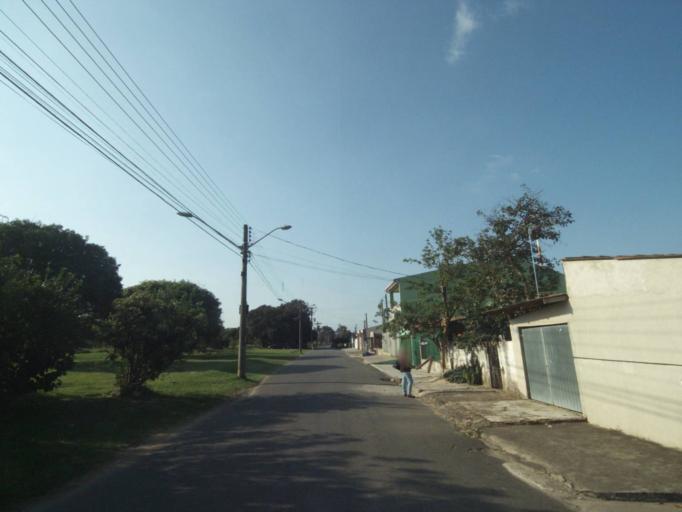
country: BR
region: Parana
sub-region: Curitiba
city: Curitiba
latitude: -25.4928
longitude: -49.3359
